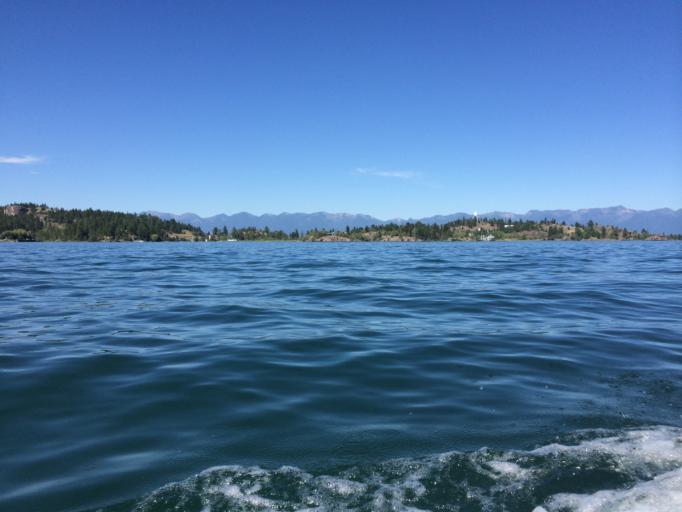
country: US
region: Montana
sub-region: Flathead County
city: Somers
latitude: 48.0694
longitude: -114.2387
